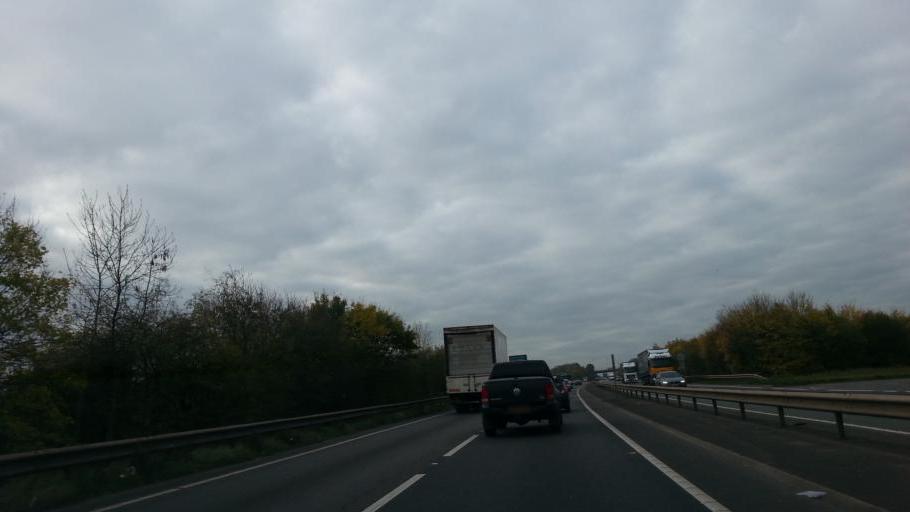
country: GB
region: England
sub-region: Leicestershire
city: Sileby
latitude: 52.6949
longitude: -1.1149
